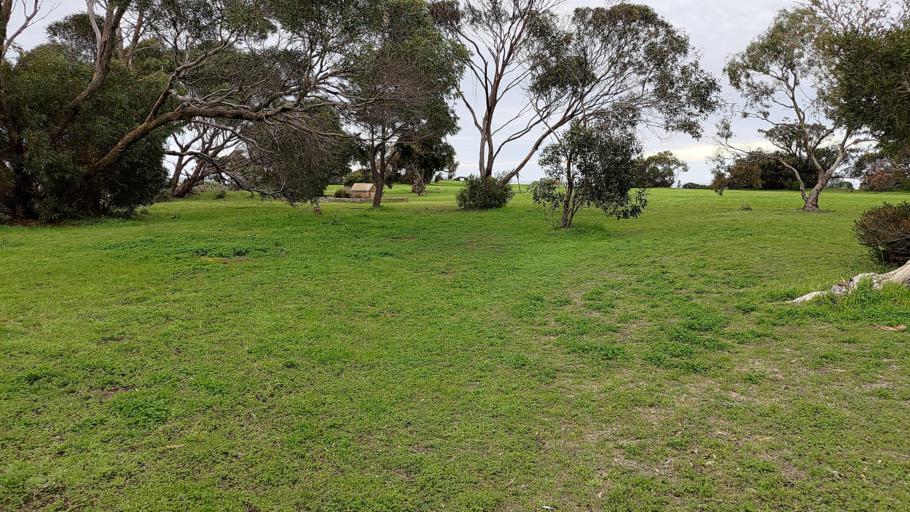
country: AU
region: South Australia
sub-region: Kangaroo Island
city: Kingscote
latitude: -35.6417
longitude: 137.6398
